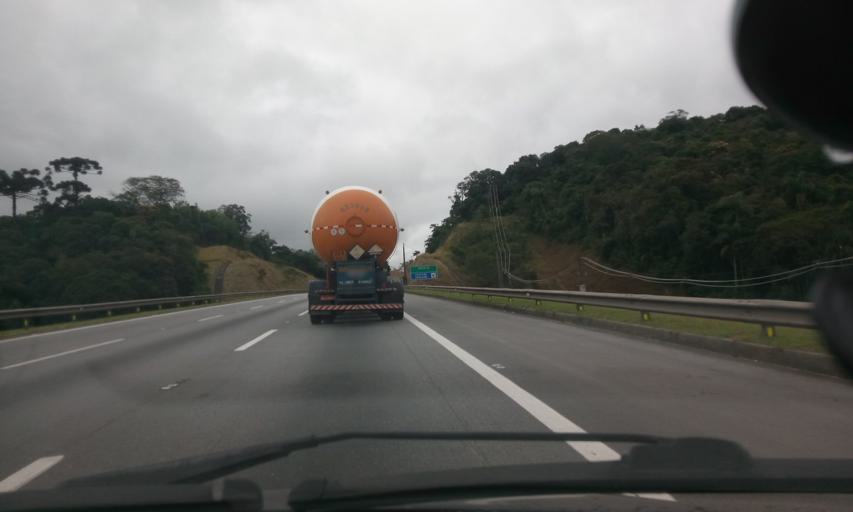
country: BR
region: Sao Paulo
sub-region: Embu
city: Embu
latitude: -23.6755
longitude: -46.8231
